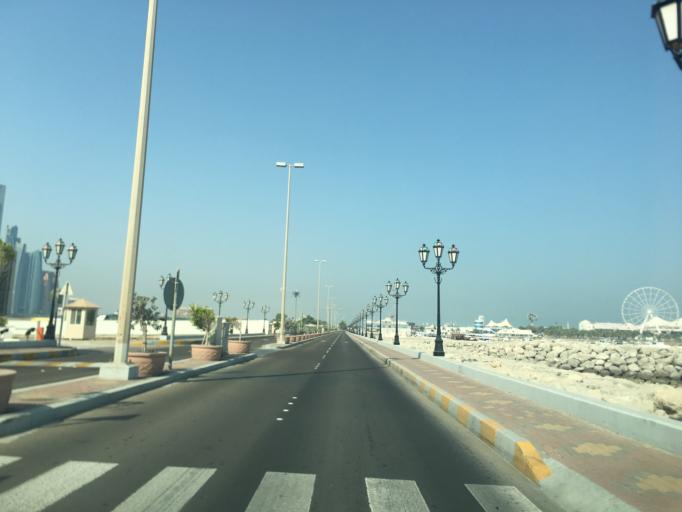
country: AE
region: Abu Dhabi
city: Abu Dhabi
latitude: 24.4766
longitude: 54.3301
